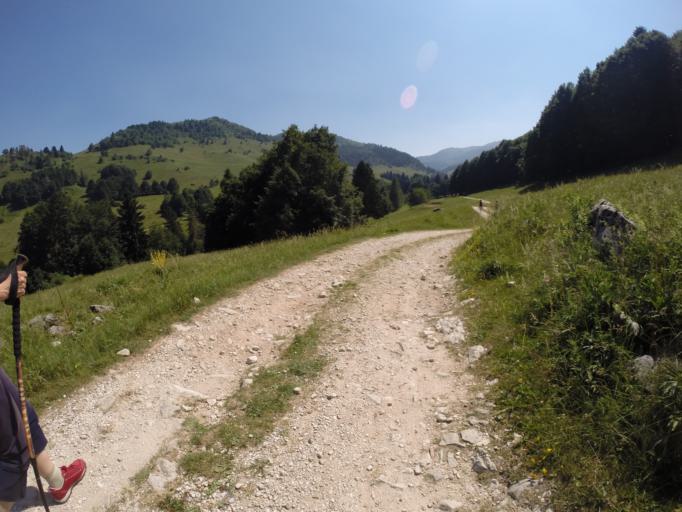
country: IT
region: Veneto
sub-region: Provincia di Treviso
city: Crespano del Grappa
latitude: 45.8992
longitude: 11.8288
